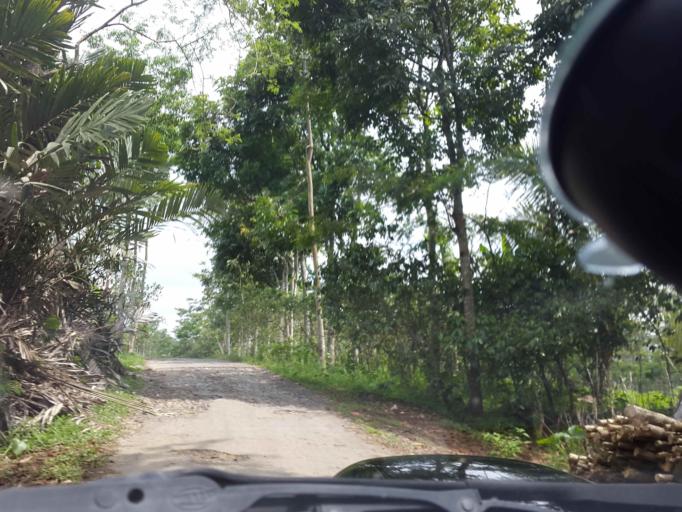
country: ID
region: Central Java
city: Wonosobo
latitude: -7.4562
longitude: 110.0120
